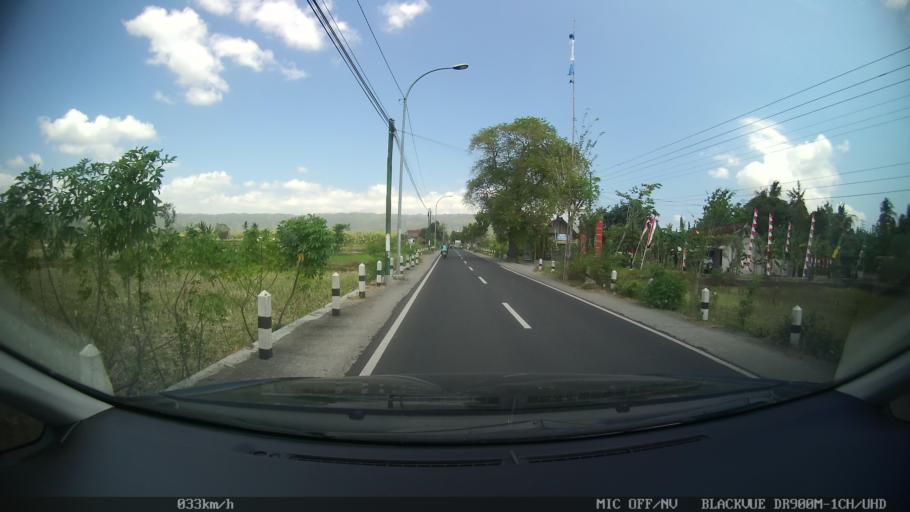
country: ID
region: Daerah Istimewa Yogyakarta
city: Pundong
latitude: -7.9283
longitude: 110.3735
